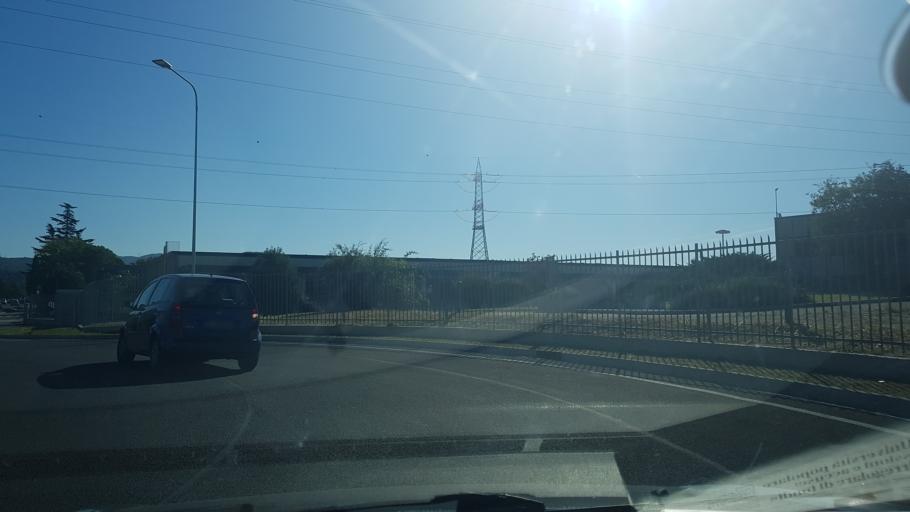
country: IT
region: Friuli Venezia Giulia
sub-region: Provincia di Gorizia
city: Monfalcone
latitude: 45.8012
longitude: 13.5598
